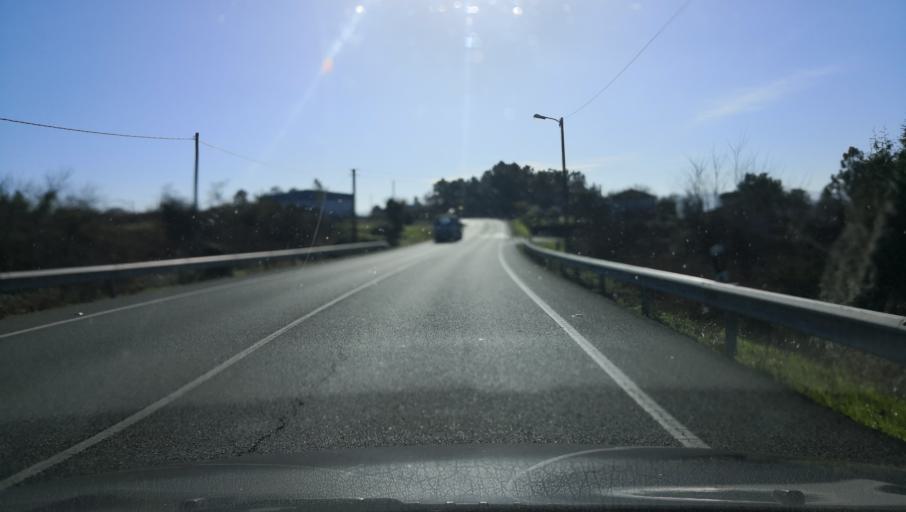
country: ES
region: Galicia
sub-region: Provincia da Coruna
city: Ribeira
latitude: 42.7829
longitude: -8.4351
